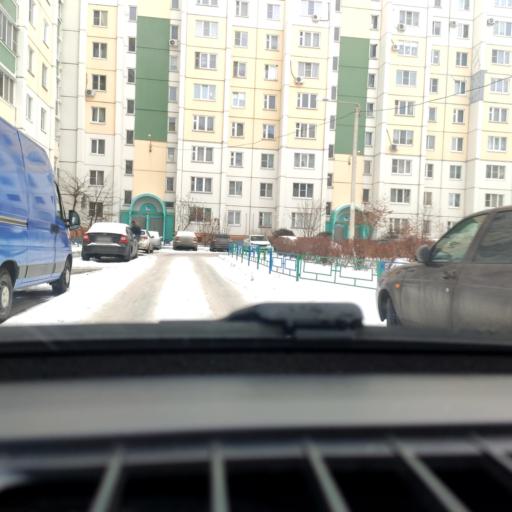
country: RU
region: Voronezj
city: Pridonskoy
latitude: 51.6200
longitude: 39.0632
